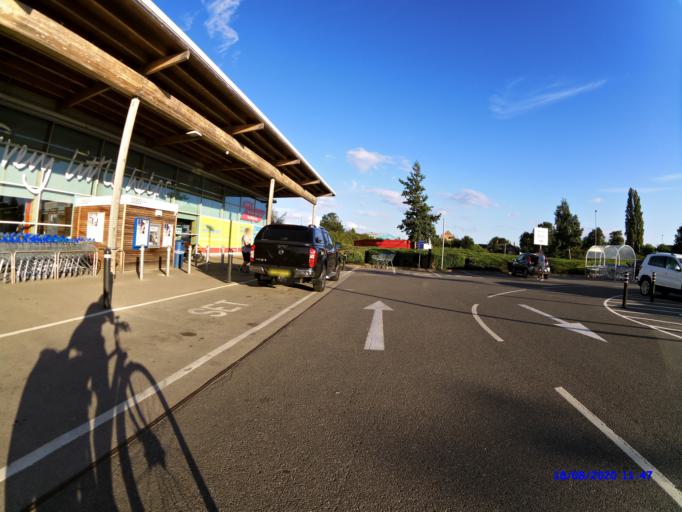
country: GB
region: England
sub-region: Cambridgeshire
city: Ramsey
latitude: 52.4557
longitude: -0.1130
